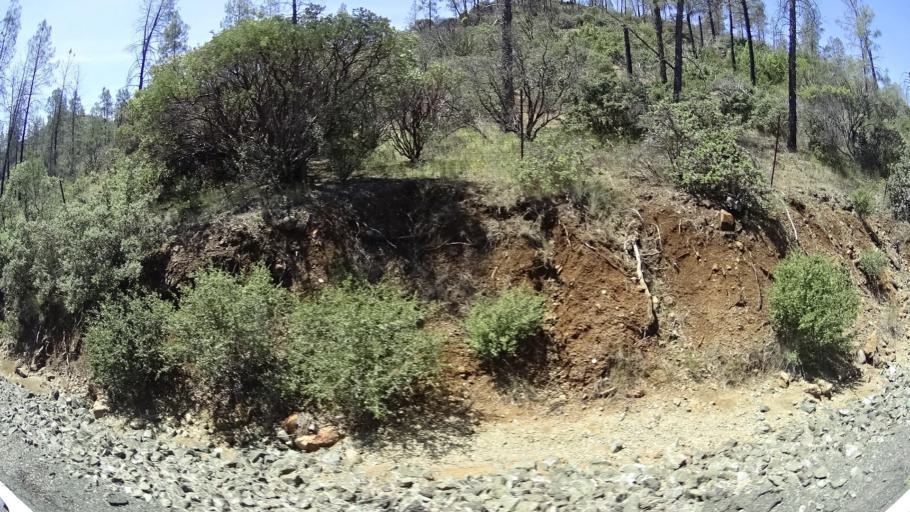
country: US
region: California
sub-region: Lake County
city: Hidden Valley Lake
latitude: 38.7178
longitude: -122.4935
